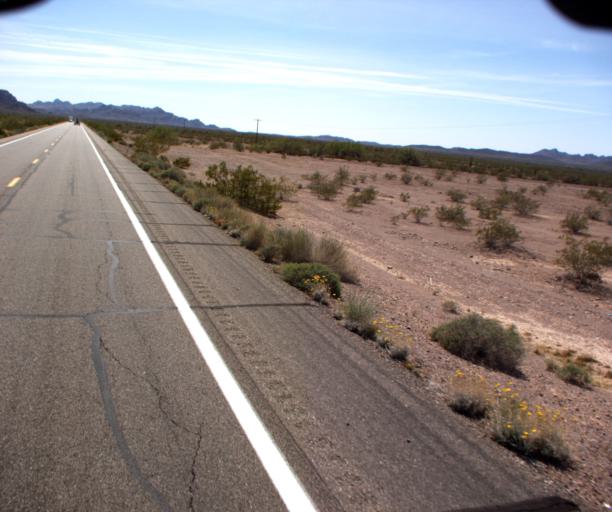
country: US
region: Arizona
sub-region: La Paz County
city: Quartzsite
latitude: 33.3224
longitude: -114.2170
